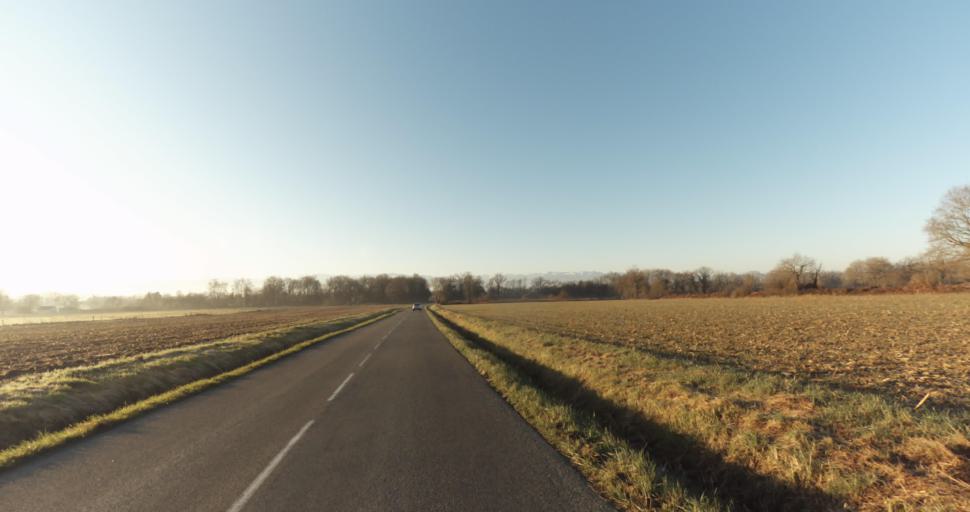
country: FR
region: Aquitaine
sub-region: Departement des Pyrenees-Atlantiques
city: Morlaas
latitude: 43.3242
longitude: -0.2734
